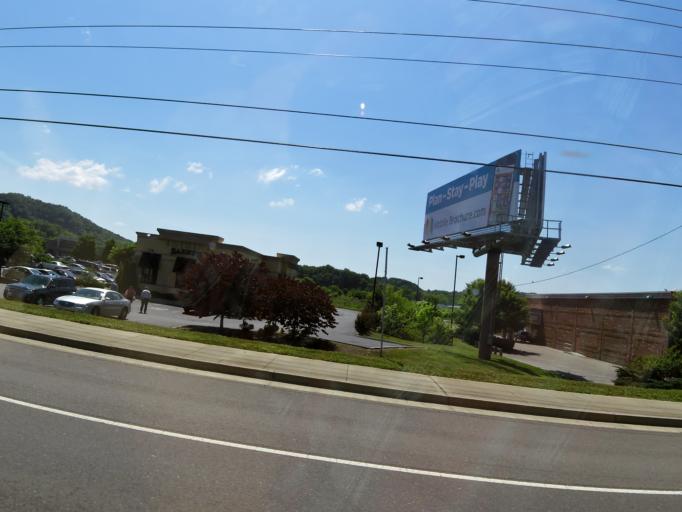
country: US
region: Tennessee
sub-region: Sevier County
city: Sevierville
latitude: 35.8809
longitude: -83.5727
